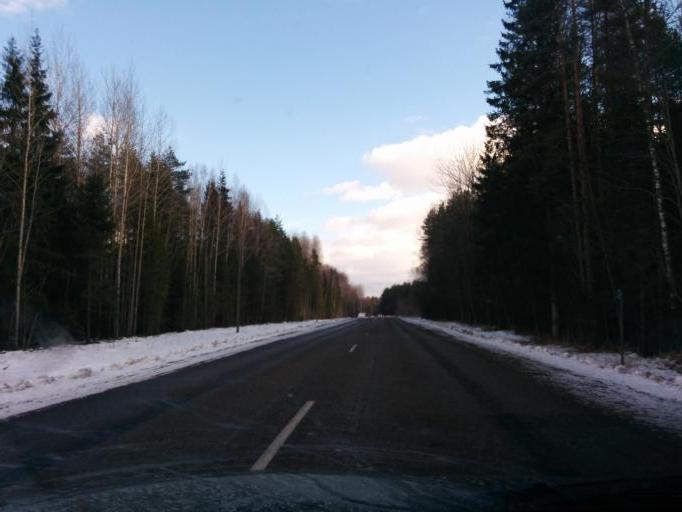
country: LV
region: Rugaju
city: Rugaji
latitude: 57.1806
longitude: 27.0796
